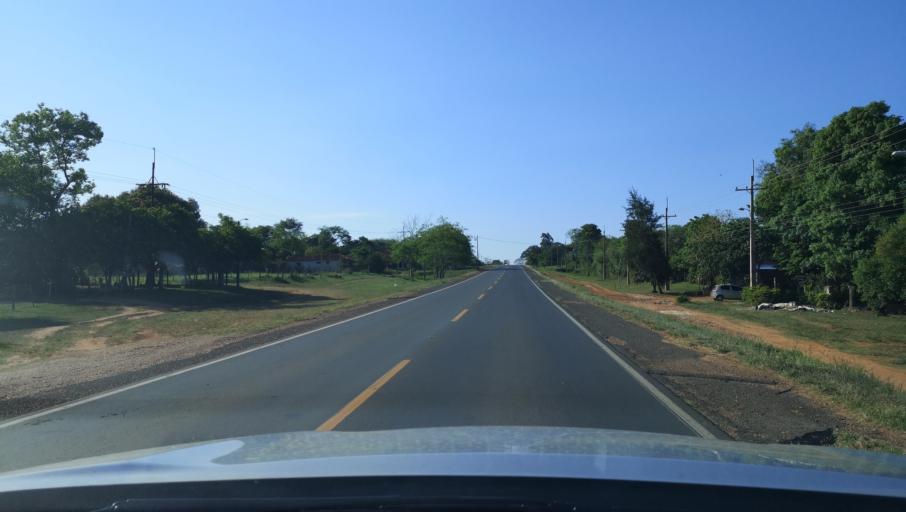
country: PY
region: Misiones
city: Santa Maria
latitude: -26.8670
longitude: -57.0331
